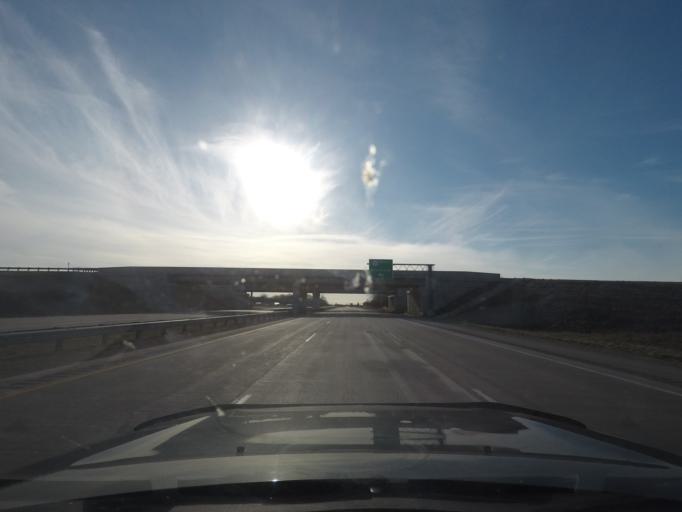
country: US
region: Indiana
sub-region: Marshall County
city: Plymouth
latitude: 41.4500
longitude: -86.2915
